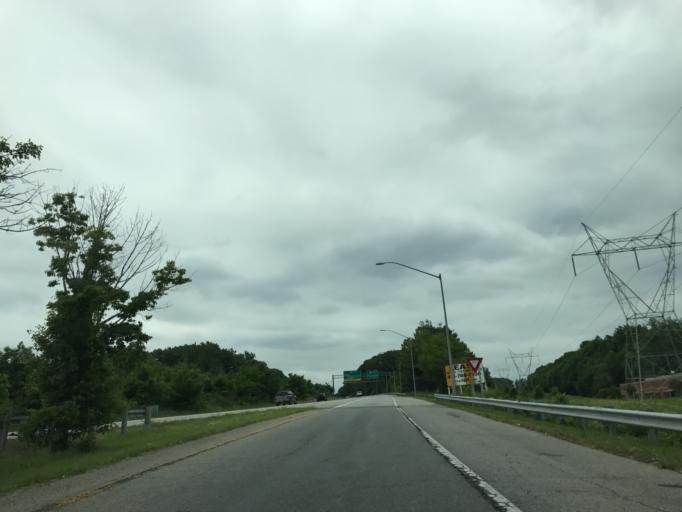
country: US
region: Maryland
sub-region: Anne Arundel County
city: Linthicum
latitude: 39.2123
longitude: -76.6801
